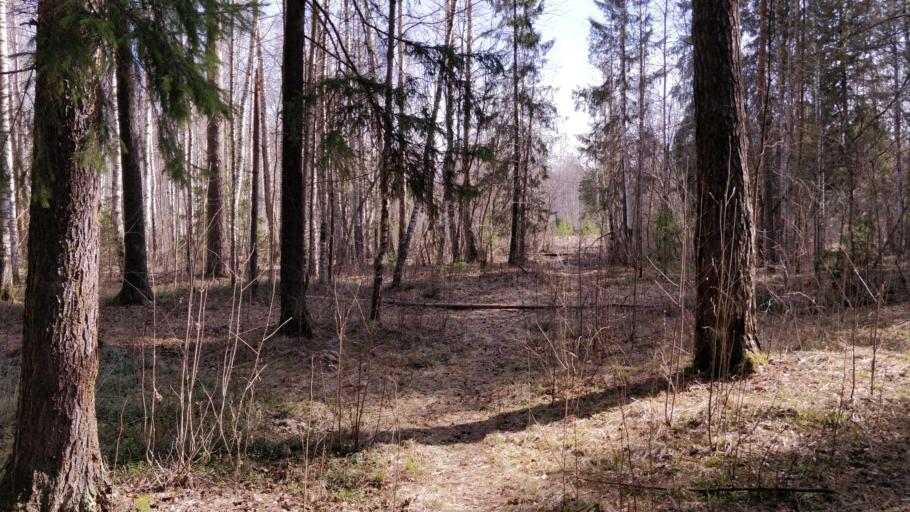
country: RU
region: Perm
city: Kondratovo
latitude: 57.9892
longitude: 56.1508
